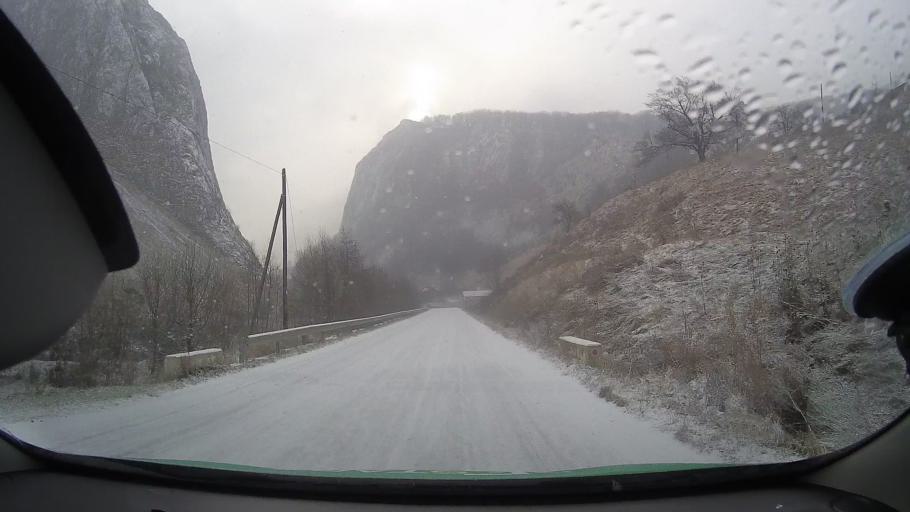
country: RO
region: Alba
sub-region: Comuna Livezile
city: Livezile
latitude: 46.3770
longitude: 23.5828
